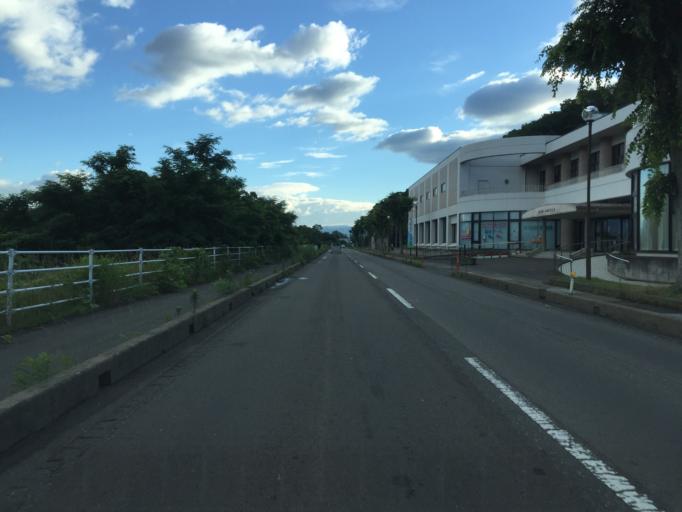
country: JP
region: Fukushima
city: Fukushima-shi
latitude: 37.7652
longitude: 140.4918
